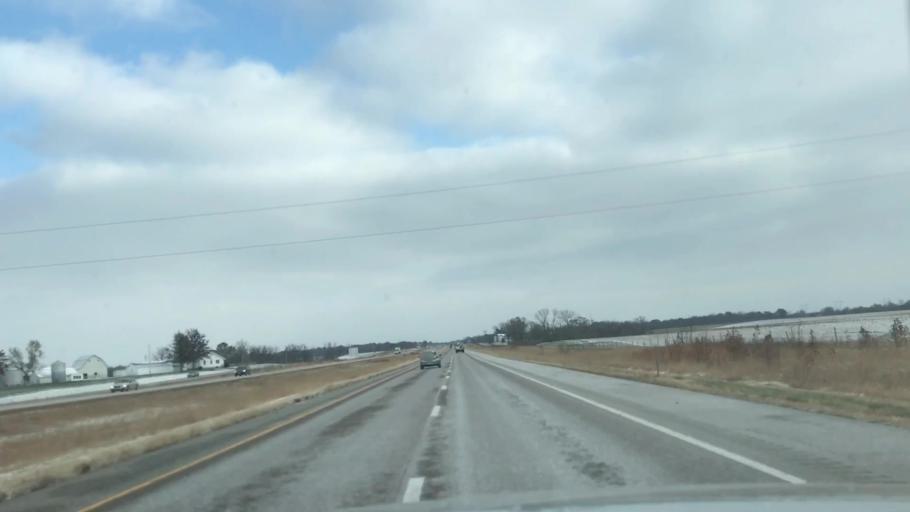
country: US
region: Illinois
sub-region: Madison County
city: Worden
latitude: 38.9446
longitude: -89.7833
